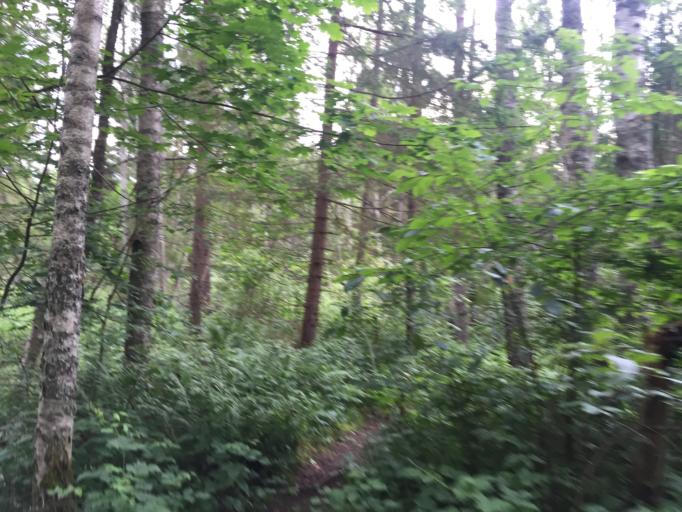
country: LV
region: Ligatne
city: Ligatne
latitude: 57.2341
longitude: 25.1533
